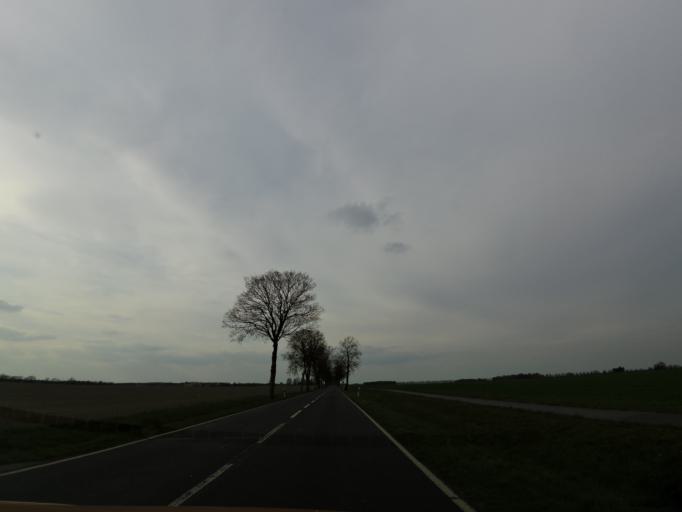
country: DE
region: Brandenburg
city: Mittenwalde
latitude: 52.2887
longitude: 13.5235
